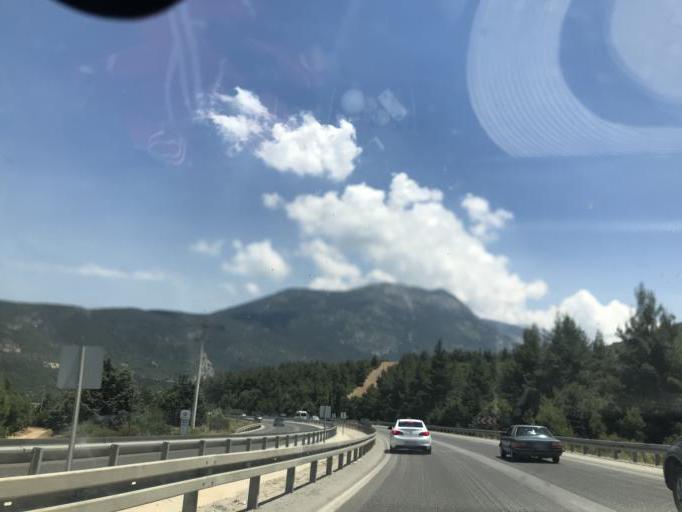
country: TR
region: Denizli
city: Honaz
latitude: 37.7304
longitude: 29.1857
